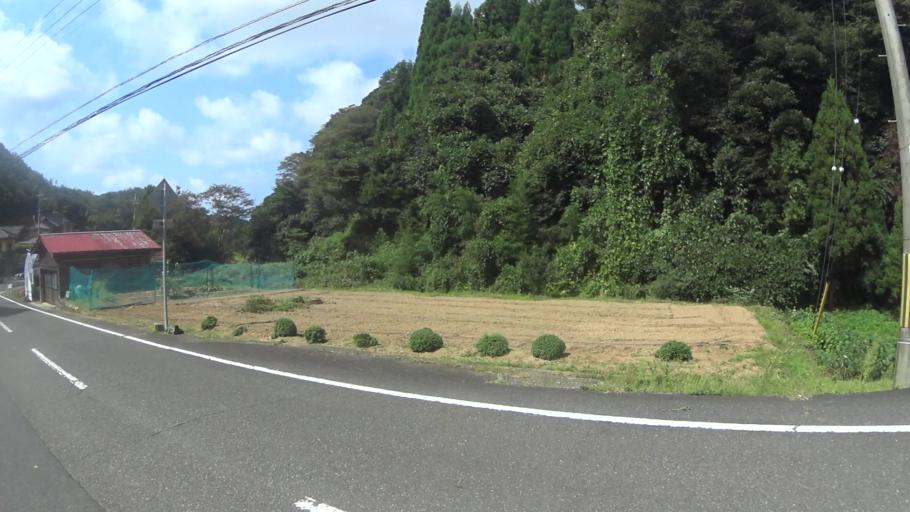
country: JP
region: Kyoto
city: Miyazu
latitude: 35.7424
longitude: 135.1846
